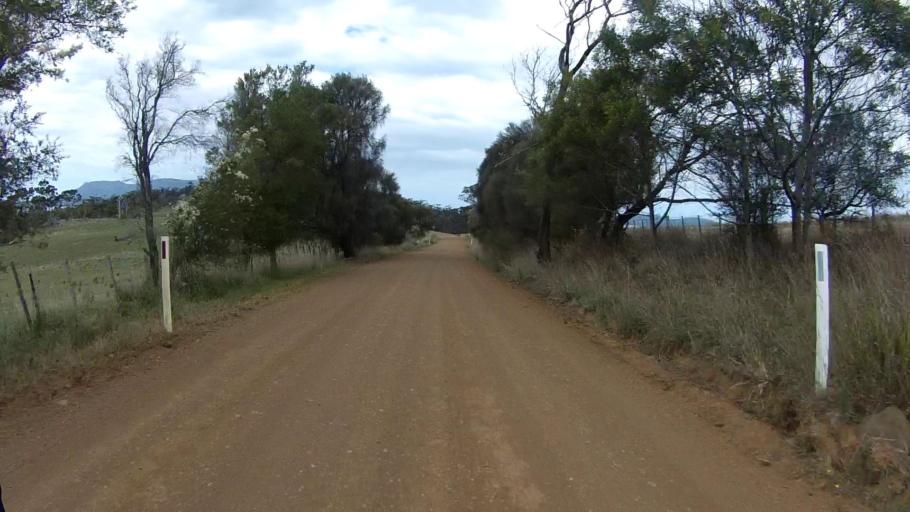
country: AU
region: Tasmania
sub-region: Sorell
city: Sorell
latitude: -42.6076
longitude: 147.9279
